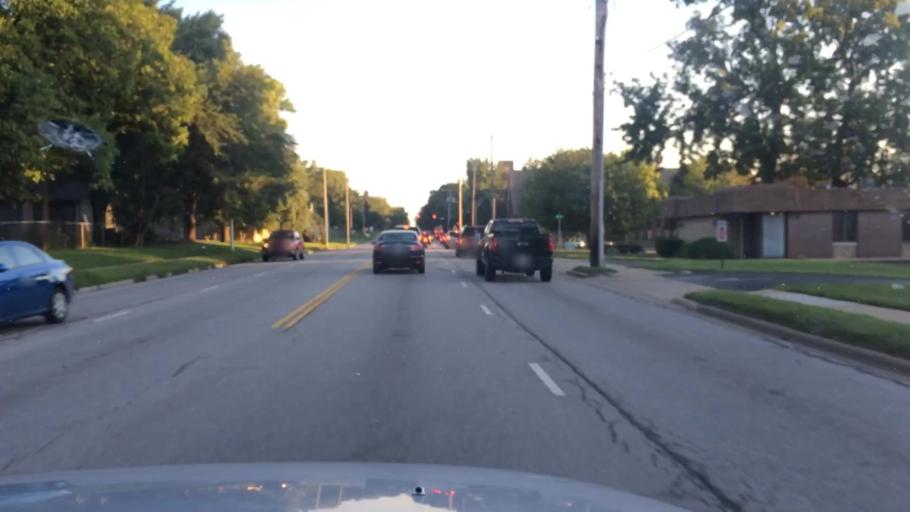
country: US
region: Kansas
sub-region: Johnson County
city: Overland Park
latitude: 38.9979
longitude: -94.6677
